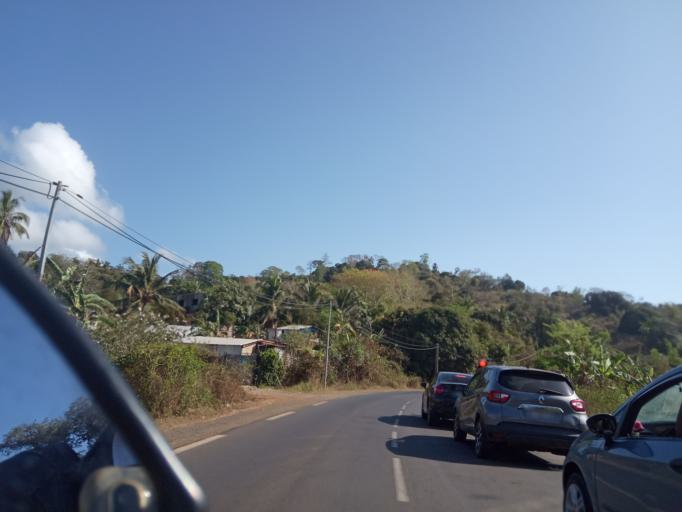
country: YT
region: Bandrele
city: Bandrele
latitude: -12.9186
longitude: 45.1839
